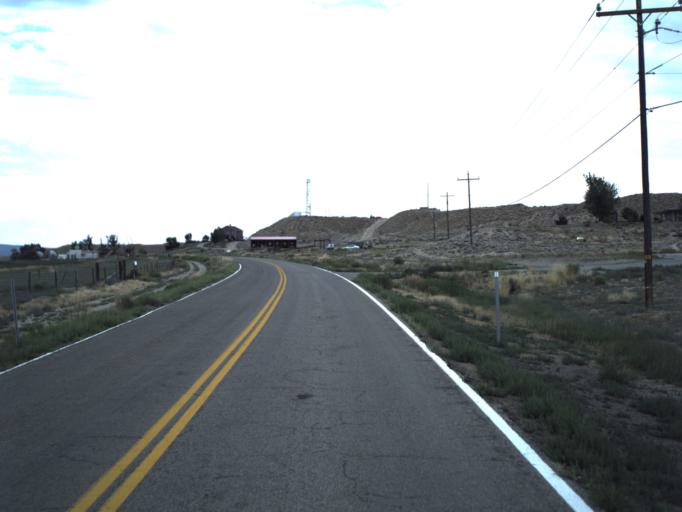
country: US
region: Utah
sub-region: Emery County
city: Huntington
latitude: 39.3735
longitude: -110.8523
